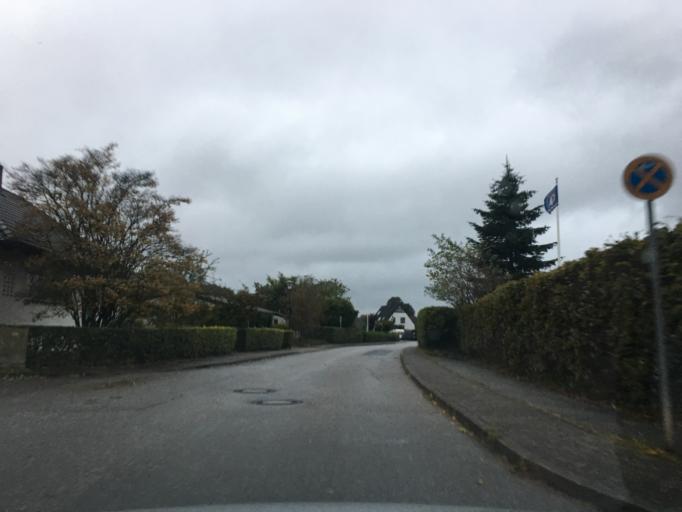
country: DE
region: Schleswig-Holstein
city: Strande
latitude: 54.4424
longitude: 10.1781
